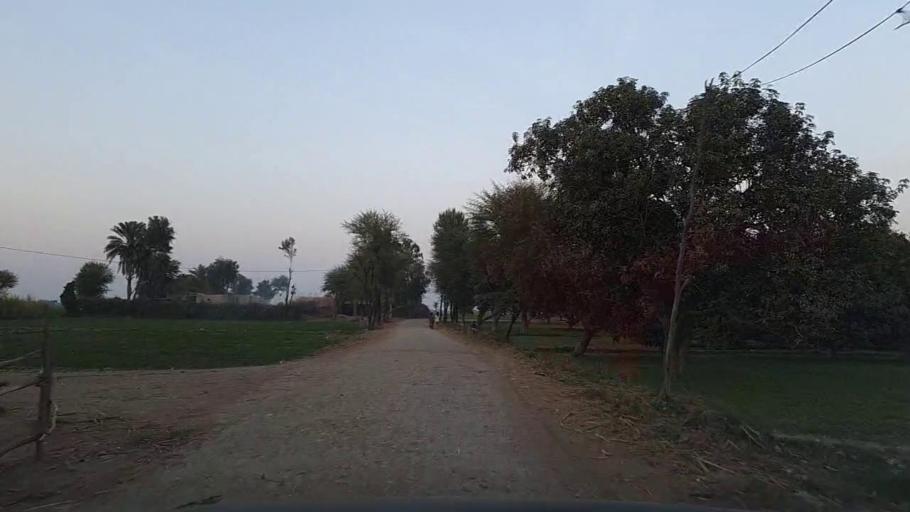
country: PK
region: Sindh
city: Tando Mittha Khan
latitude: 25.9442
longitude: 69.1450
